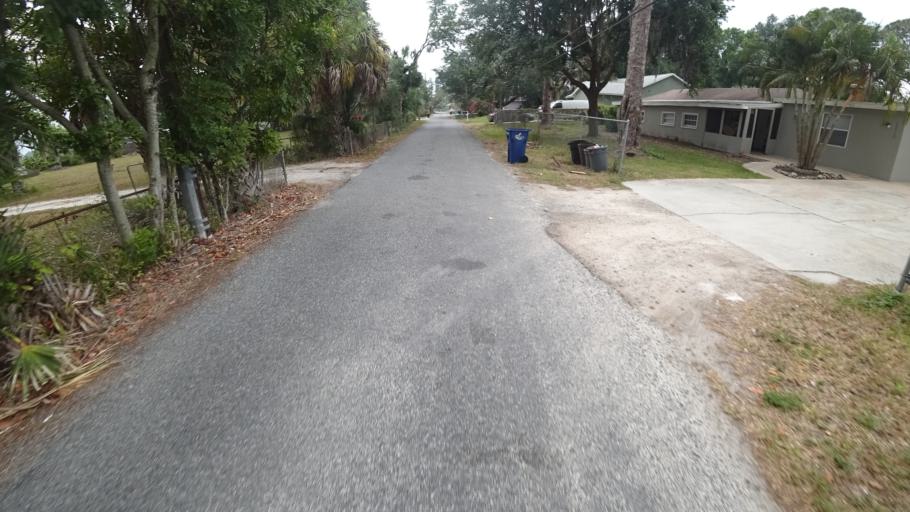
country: US
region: Florida
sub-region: Manatee County
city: Samoset
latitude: 27.4792
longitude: -82.5025
